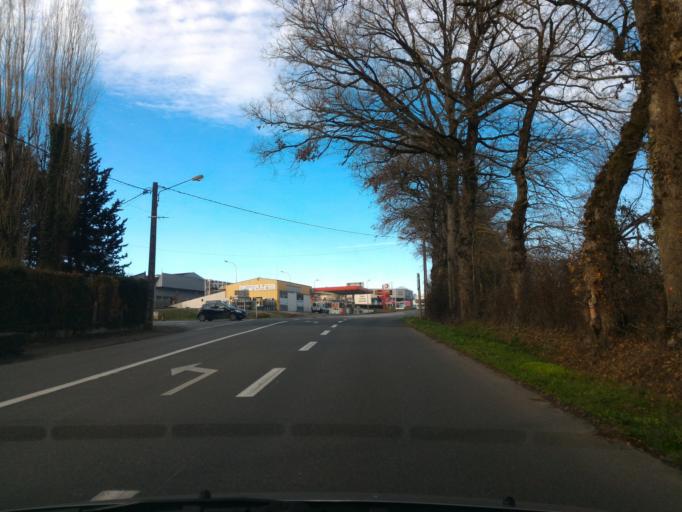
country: FR
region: Poitou-Charentes
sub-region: Departement de la Charente
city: Confolens
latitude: 46.0207
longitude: 0.6604
